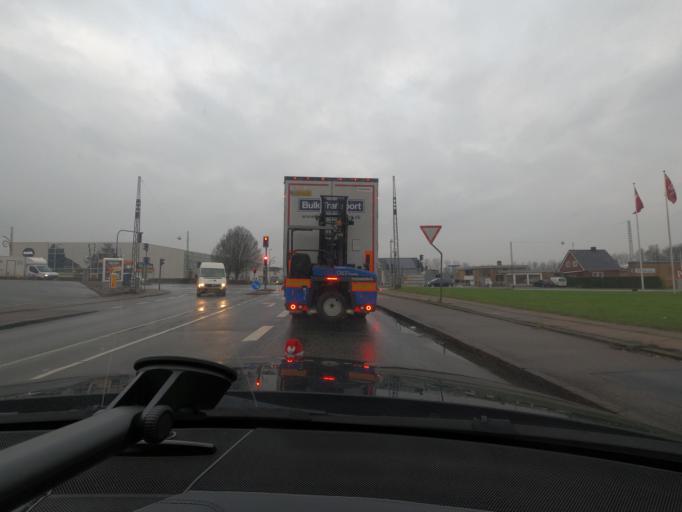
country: DK
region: South Denmark
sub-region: Sonderborg Kommune
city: Sonderborg
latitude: 54.9192
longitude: 9.8098
